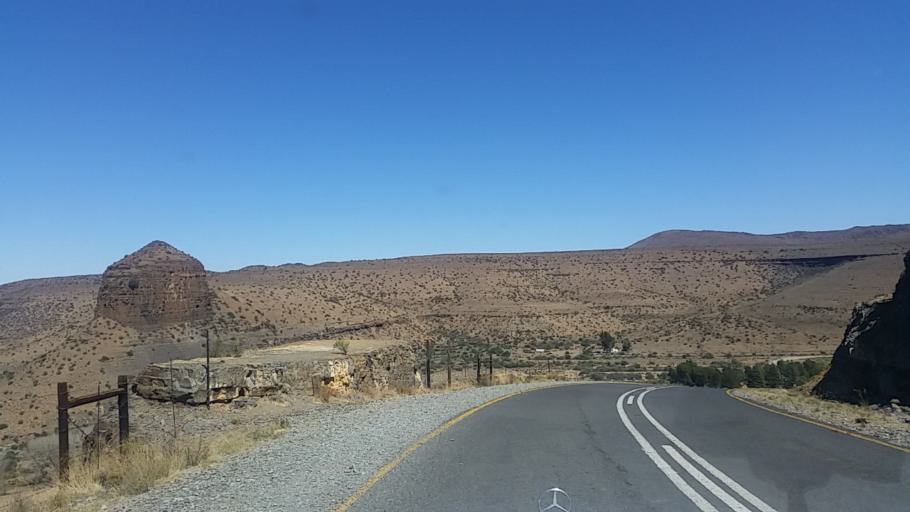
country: ZA
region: Eastern Cape
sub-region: Cacadu District Municipality
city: Graaff-Reinet
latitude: -31.8945
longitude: 24.5767
